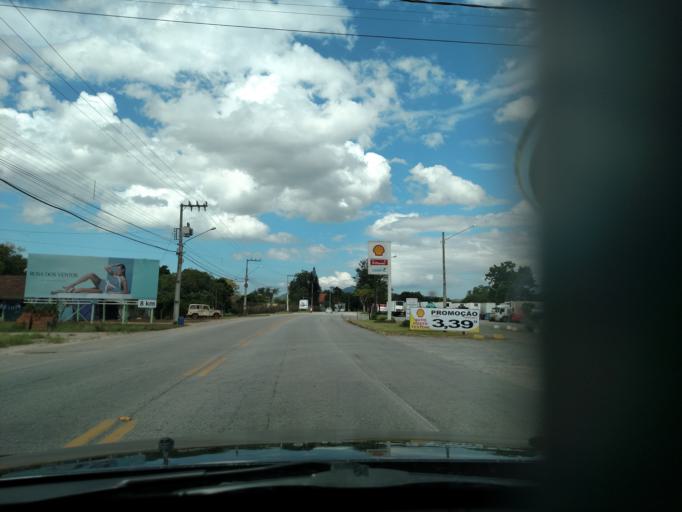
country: BR
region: Santa Catarina
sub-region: Gaspar
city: Gaspar
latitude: -26.9116
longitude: -48.9183
